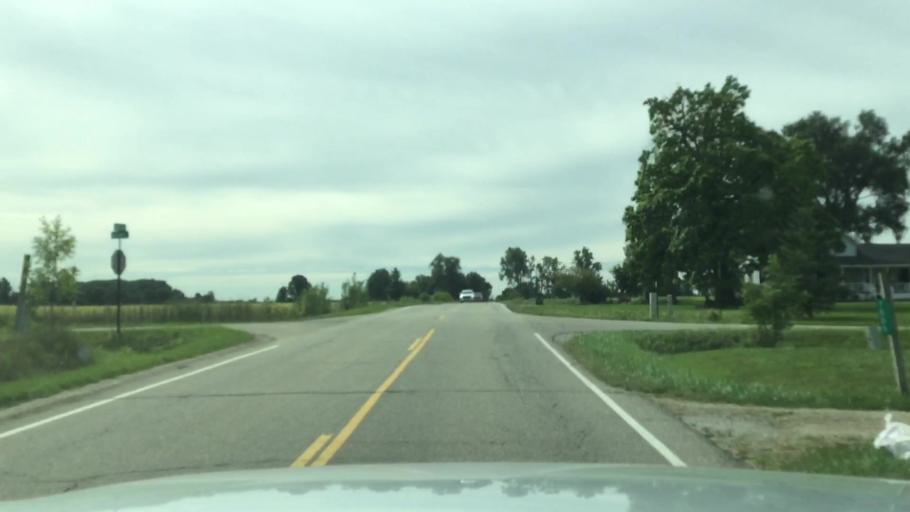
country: US
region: Michigan
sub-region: Genesee County
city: Montrose
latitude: 43.1024
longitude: -83.9877
